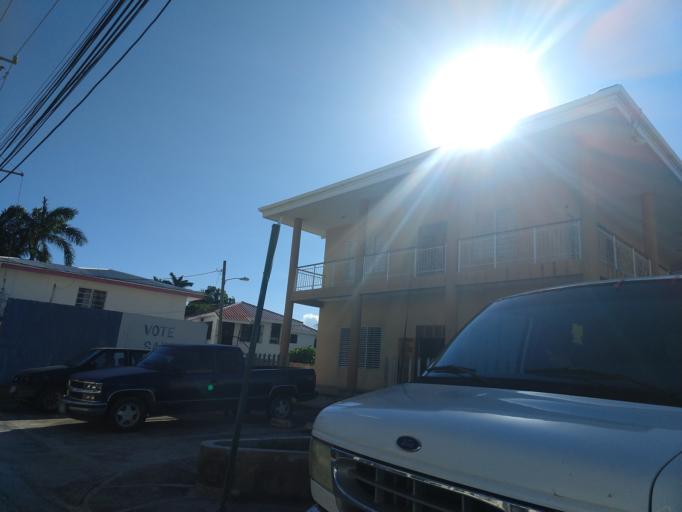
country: BZ
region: Belize
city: Belize City
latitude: 17.4976
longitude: -88.1837
